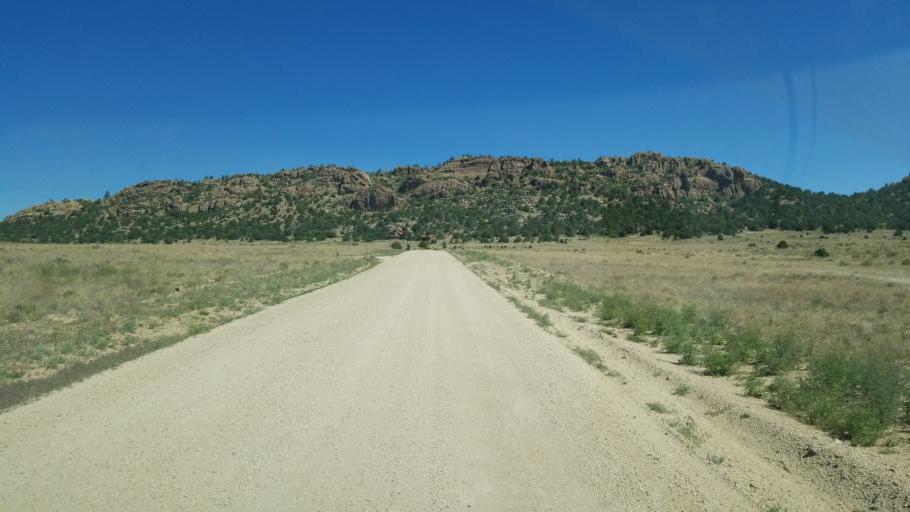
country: US
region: Colorado
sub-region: Custer County
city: Westcliffe
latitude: 38.2312
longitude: -105.4571
